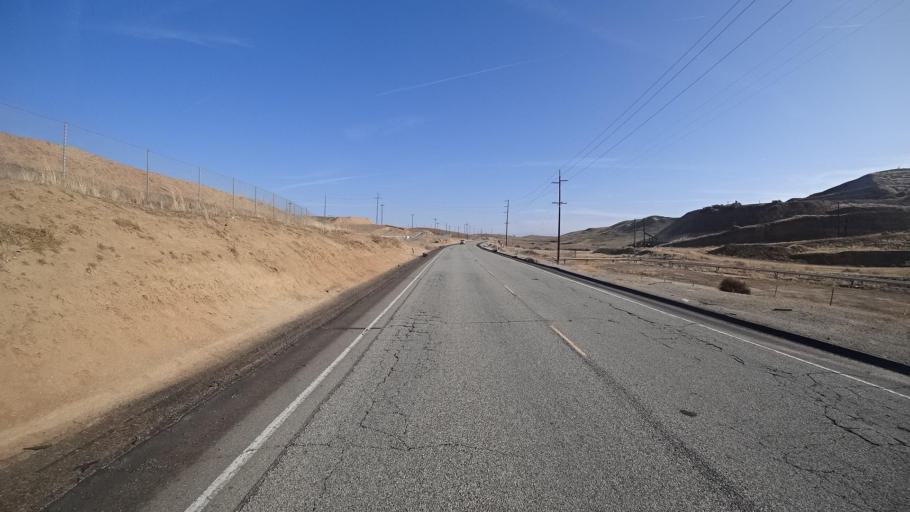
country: US
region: California
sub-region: Kern County
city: Oildale
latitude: 35.4881
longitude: -119.0046
